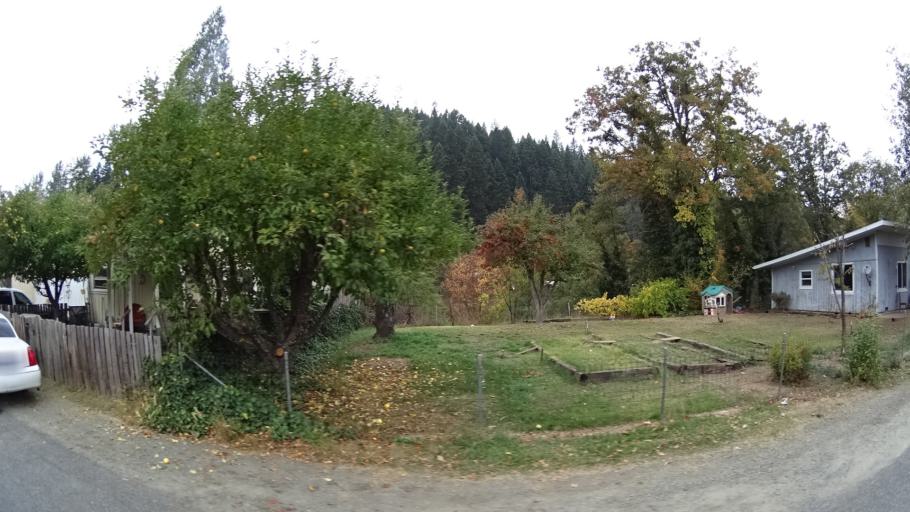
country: US
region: California
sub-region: Siskiyou County
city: Happy Camp
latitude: 41.7963
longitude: -123.3783
